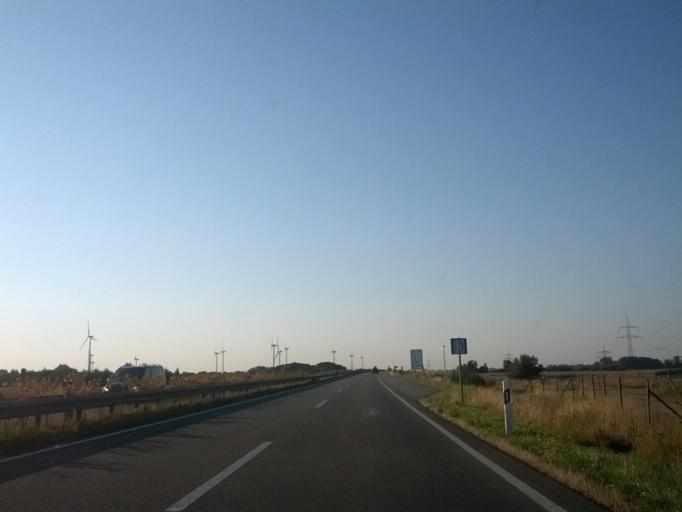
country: DE
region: Mecklenburg-Vorpommern
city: Brandshagen
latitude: 54.1813
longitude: 13.1694
